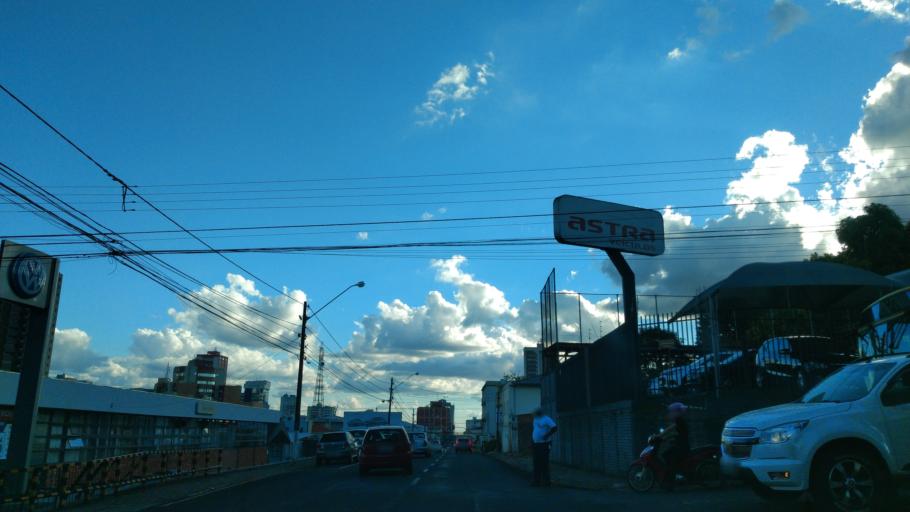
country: BR
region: Parana
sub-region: Guarapuava
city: Guarapuava
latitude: -25.3888
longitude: -51.4643
